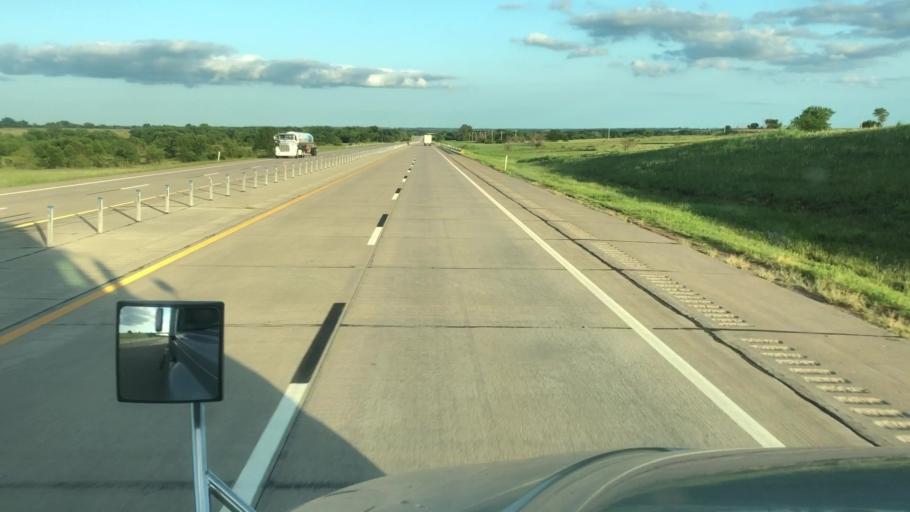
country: US
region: Oklahoma
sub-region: Pawnee County
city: Pawnee
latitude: 36.3328
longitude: -97.0143
